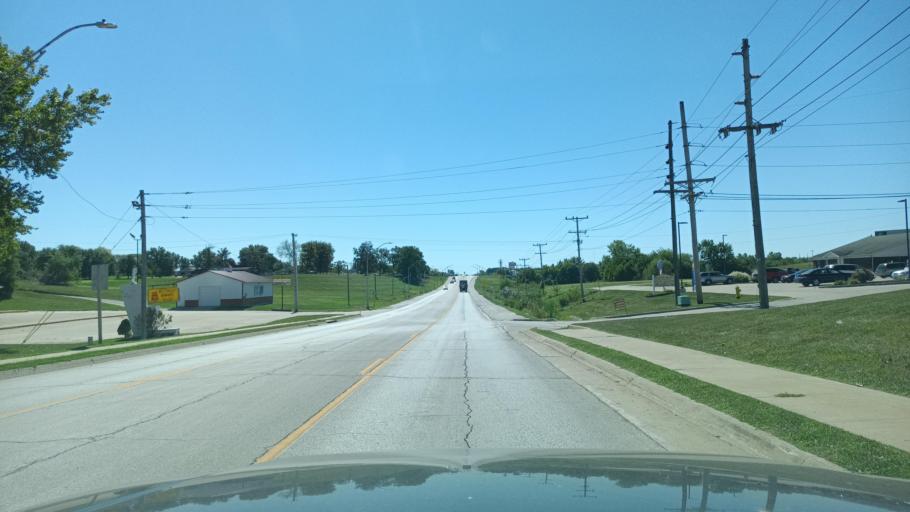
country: US
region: Missouri
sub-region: Adair County
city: Kirksville
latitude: 40.1757
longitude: -92.5720
